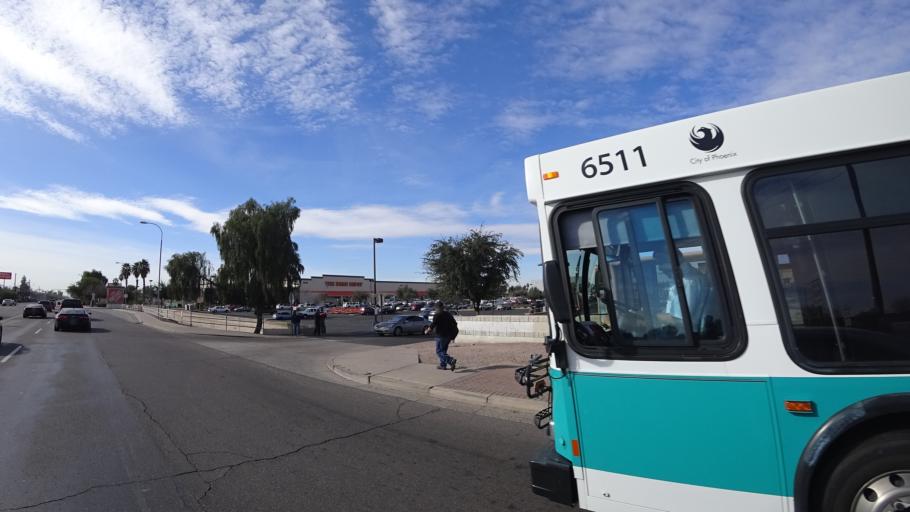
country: US
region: Arizona
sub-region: Maricopa County
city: Glendale
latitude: 33.5087
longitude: -112.1517
